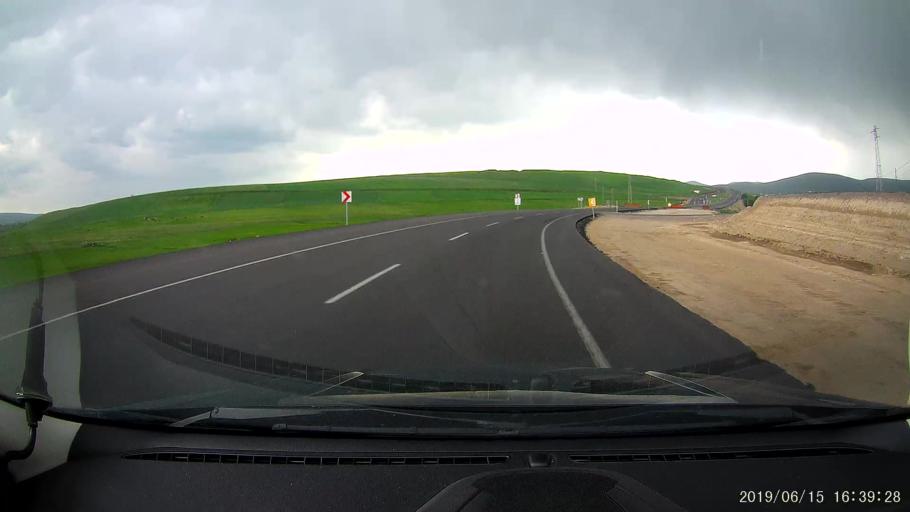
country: TR
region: Ardahan
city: Haskoy
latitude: 40.9826
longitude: 42.8973
